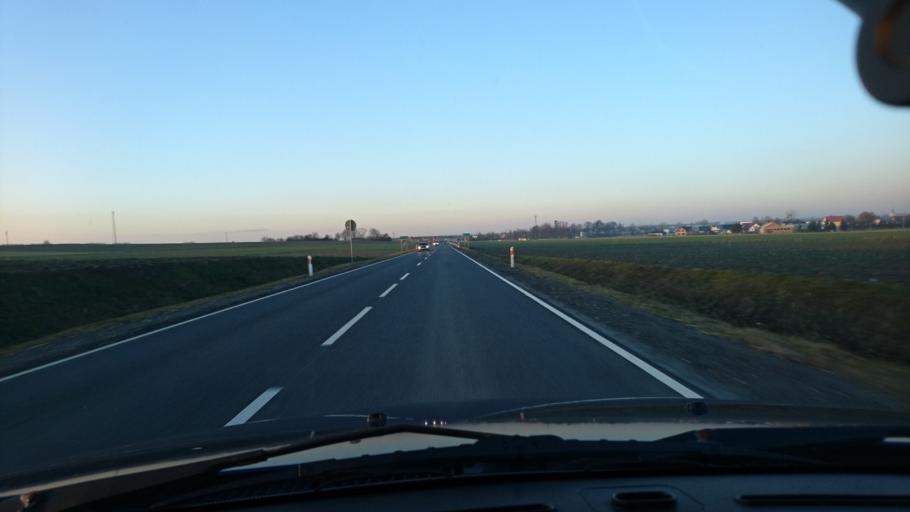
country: PL
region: Silesian Voivodeship
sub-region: Powiat gliwicki
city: Wielowies
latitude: 50.4975
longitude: 18.6065
